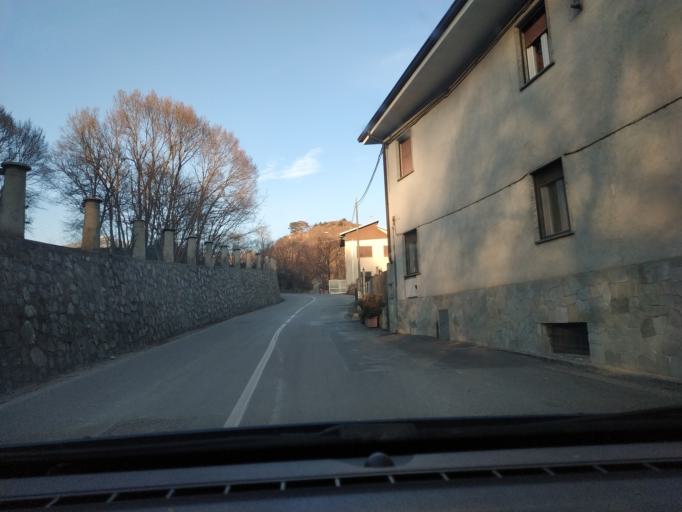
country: IT
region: Piedmont
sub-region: Provincia di Torino
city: Ivrea
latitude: 45.4773
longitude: 7.8709
